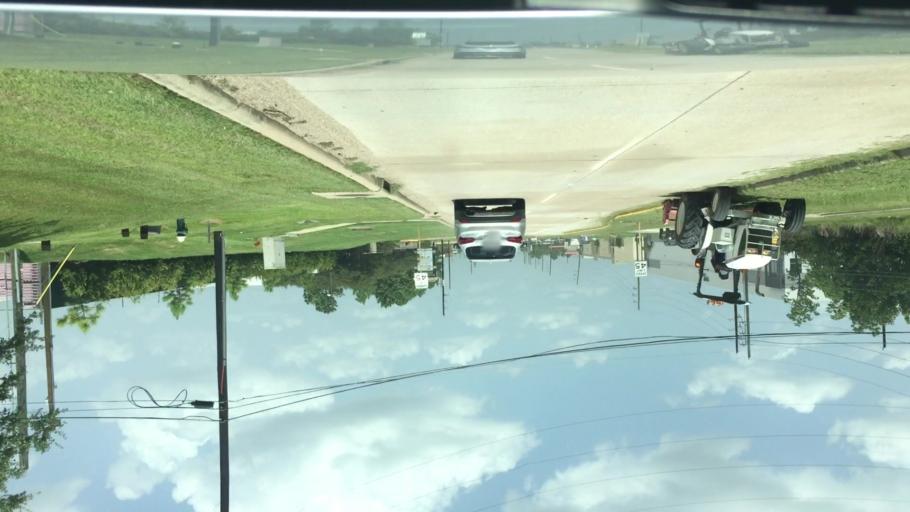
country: US
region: Texas
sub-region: Harris County
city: Hudson
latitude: 29.9516
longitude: -95.5214
